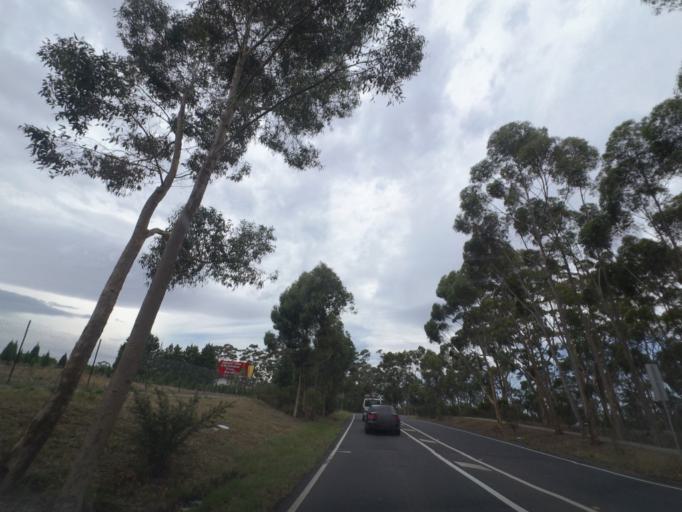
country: AU
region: Victoria
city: Saint Helena
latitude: -37.6838
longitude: 145.1367
